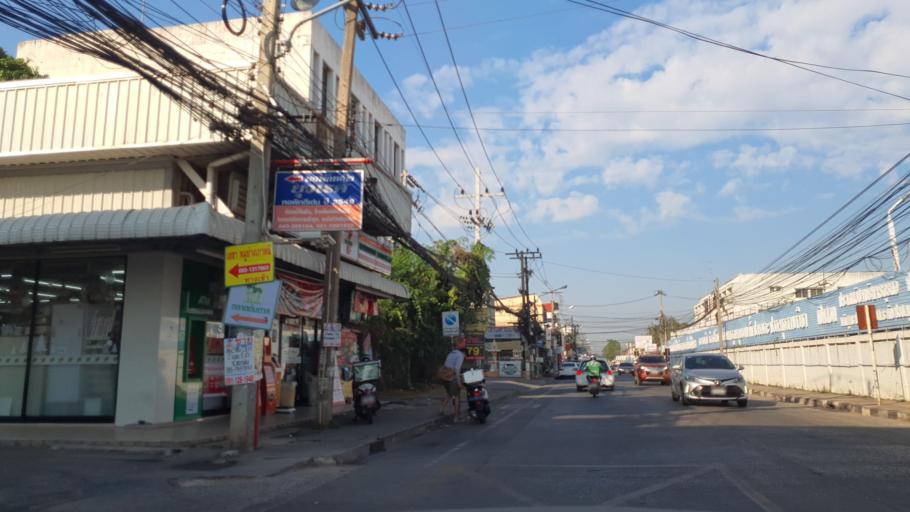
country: TH
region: Khon Kaen
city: Khon Kaen
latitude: 16.4214
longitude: 102.8187
